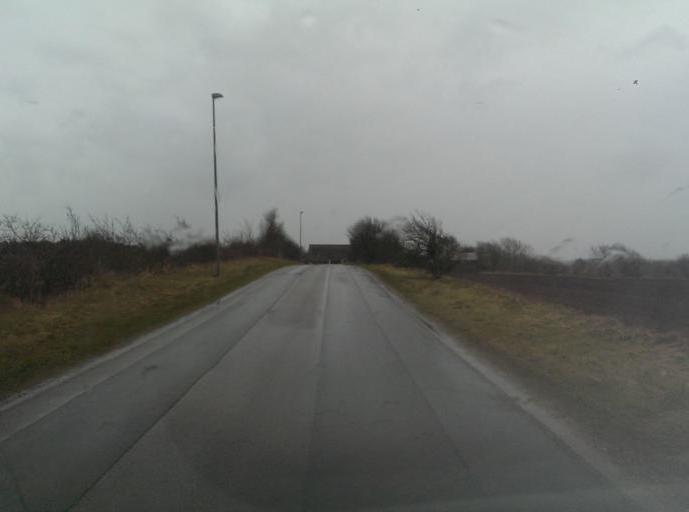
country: DK
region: Central Jutland
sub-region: Ringkobing-Skjern Kommune
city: Skjern
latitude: 56.0062
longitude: 8.4171
